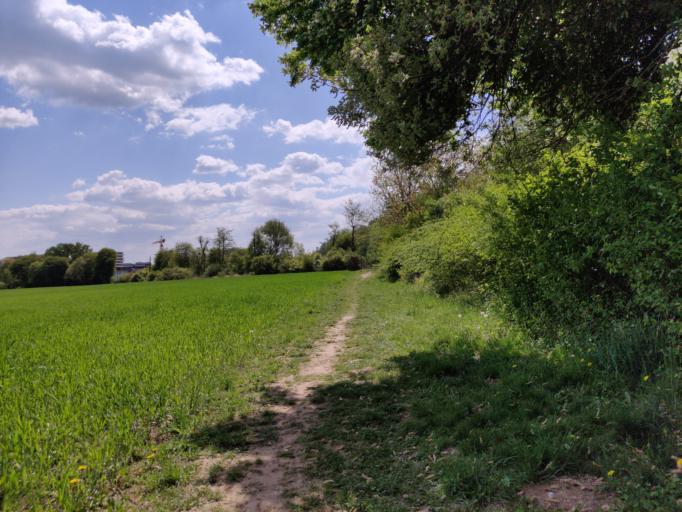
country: AT
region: Styria
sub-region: Graz Stadt
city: Wetzelsdorf
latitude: 47.0411
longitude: 15.3876
